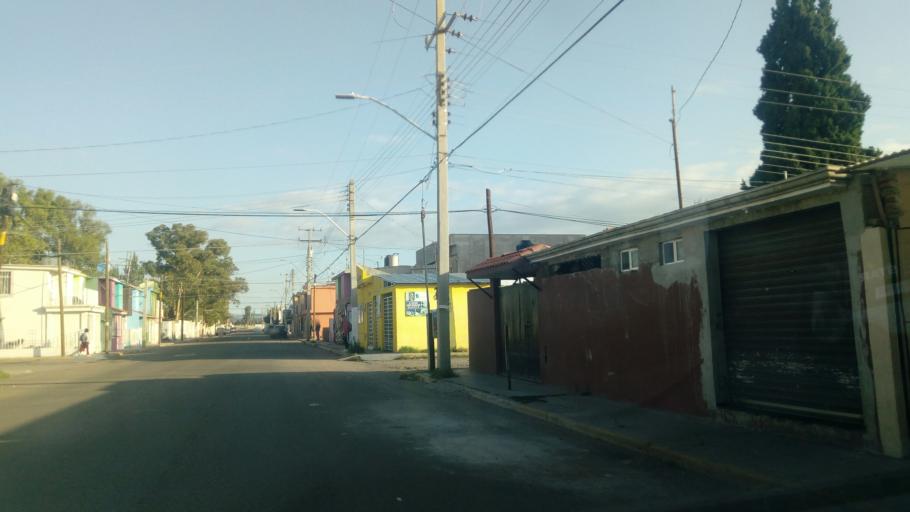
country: MX
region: Durango
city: Victoria de Durango
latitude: 24.0482
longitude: -104.6182
